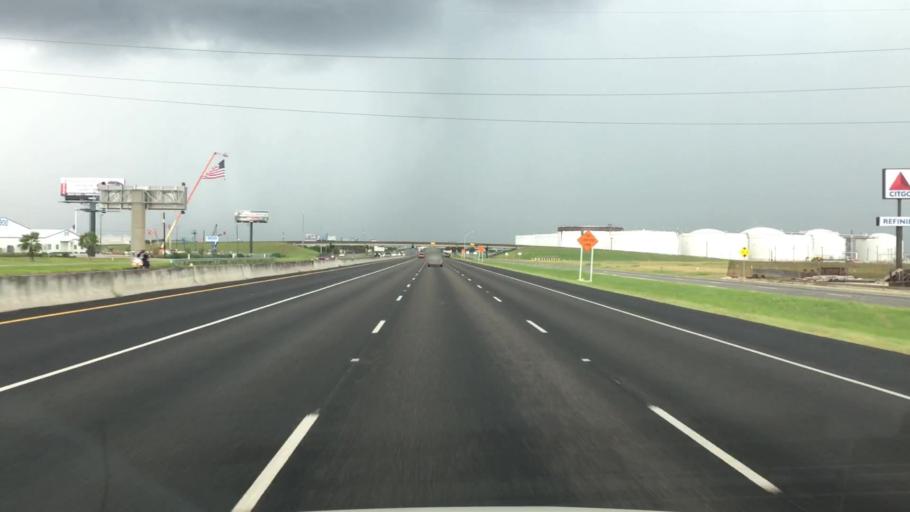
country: US
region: Texas
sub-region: Nueces County
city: Corpus Christi
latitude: 27.8096
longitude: -97.4987
